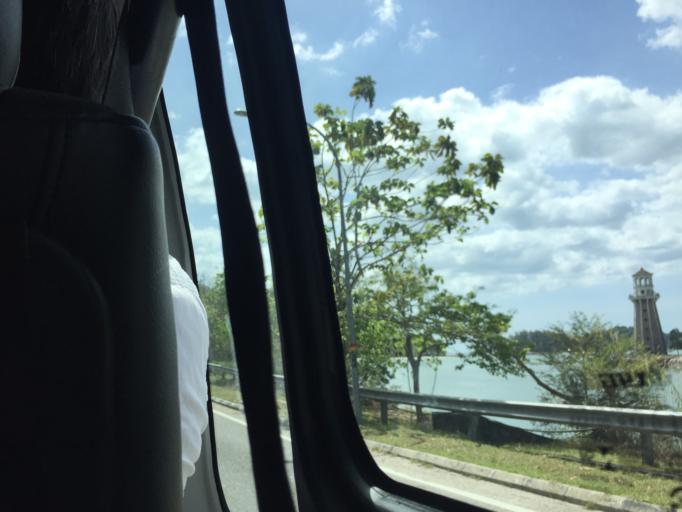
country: MY
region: Kedah
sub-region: Langkawi
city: Kuah
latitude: 6.3643
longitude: 99.6852
